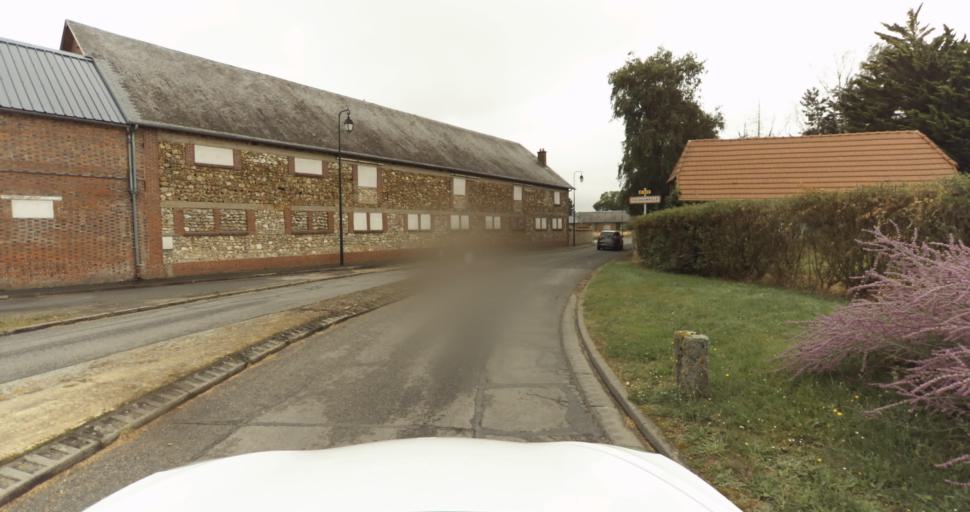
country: FR
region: Haute-Normandie
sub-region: Departement de l'Eure
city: Aviron
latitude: 49.0856
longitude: 1.0707
